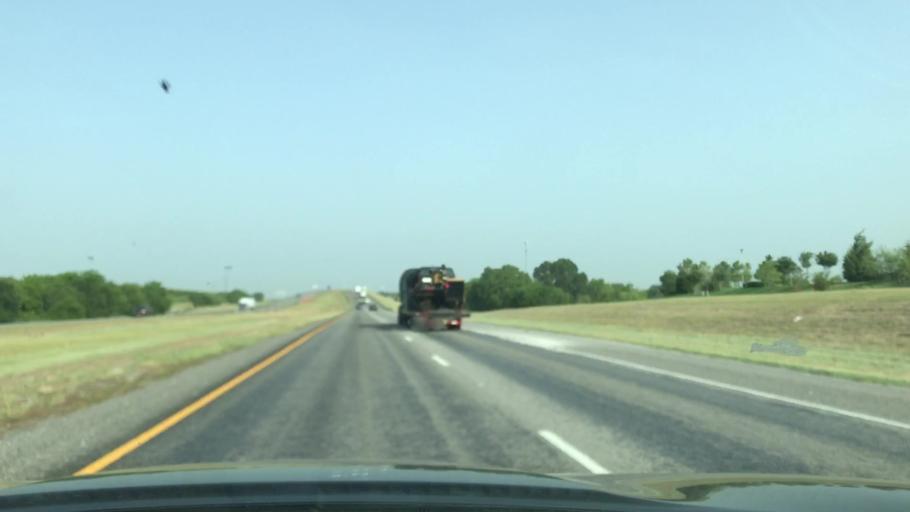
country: US
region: Texas
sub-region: Kaufman County
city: Talty
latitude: 32.7345
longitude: -96.3485
